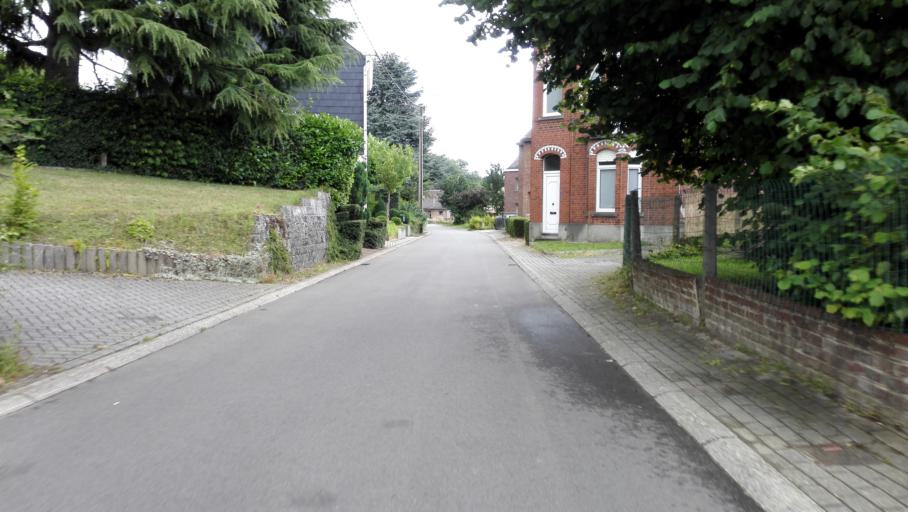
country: BE
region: Flanders
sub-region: Provincie Vlaams-Brabant
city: Bertem
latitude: 50.8508
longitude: 4.5822
